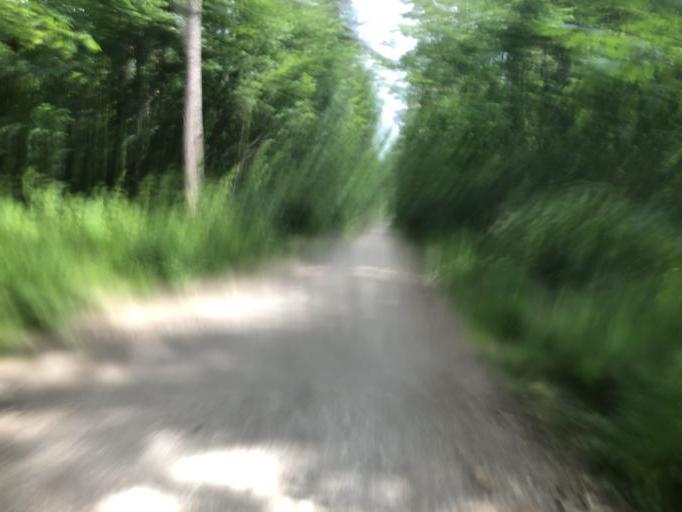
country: DE
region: Bavaria
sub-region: Regierungsbezirk Mittelfranken
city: Mohrendorf
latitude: 49.6121
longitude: 10.9630
